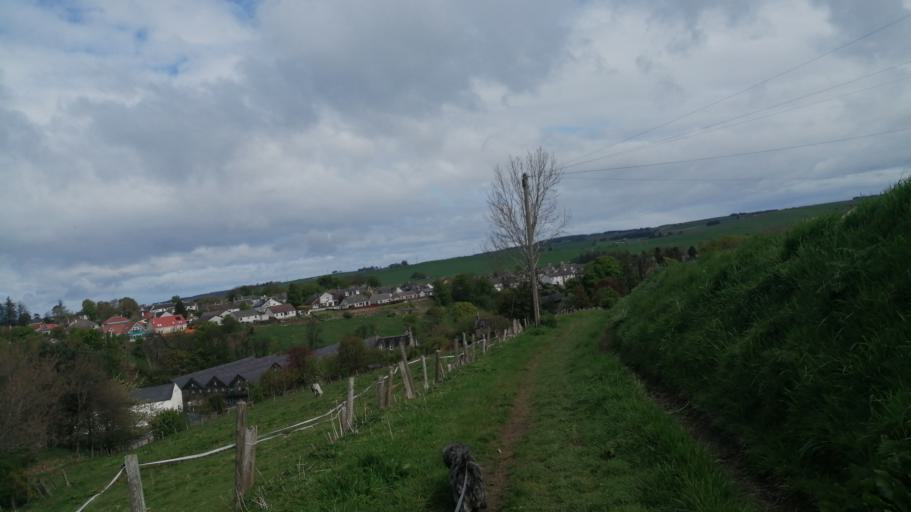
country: GB
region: Scotland
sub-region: Moray
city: Keith
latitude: 57.5389
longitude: -2.9590
